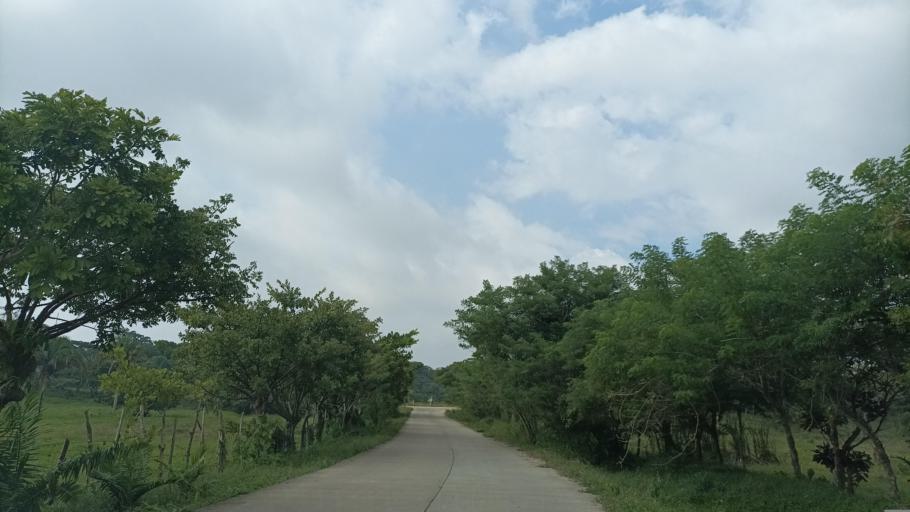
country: MX
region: Veracruz
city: Allende
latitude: 18.0956
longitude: -94.2932
